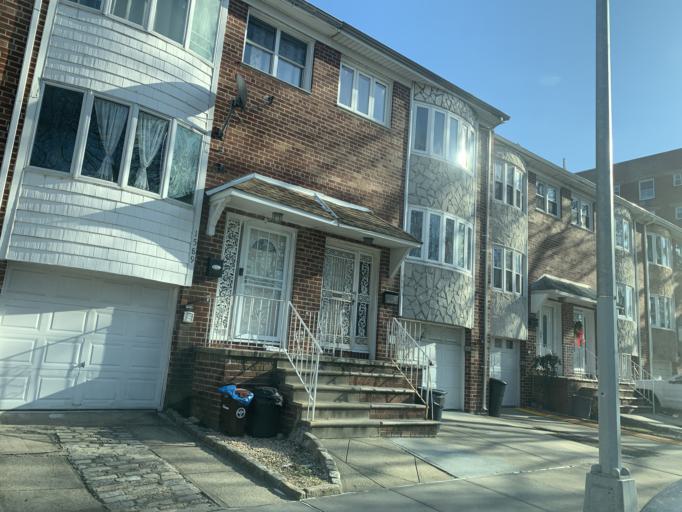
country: US
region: New York
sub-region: Nassau County
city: East Atlantic Beach
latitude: 40.7833
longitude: -73.8224
